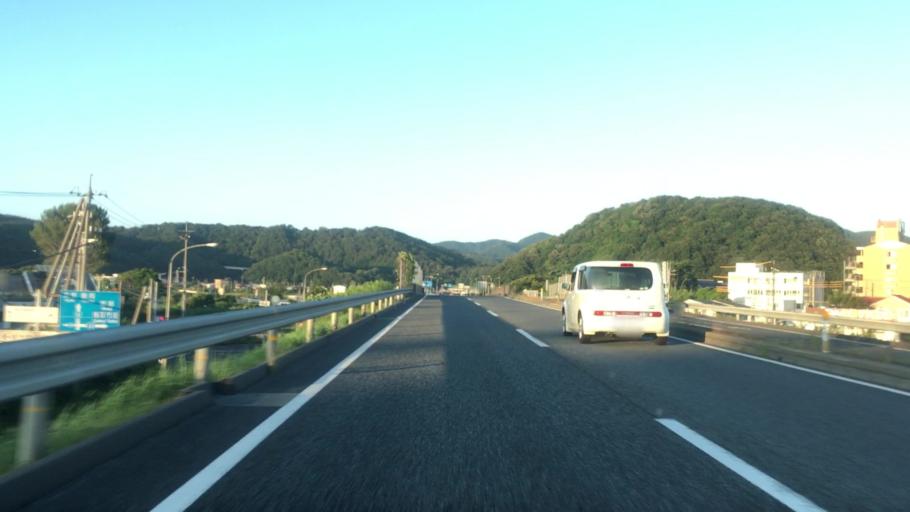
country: JP
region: Tottori
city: Tottori
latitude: 35.5218
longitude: 134.2154
